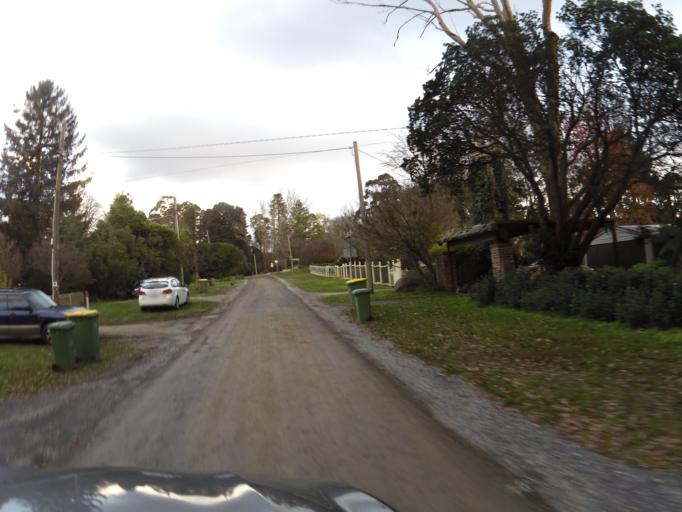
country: AU
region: Victoria
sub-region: Yarra Ranges
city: Ferny Creek
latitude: -37.8691
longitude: 145.3417
